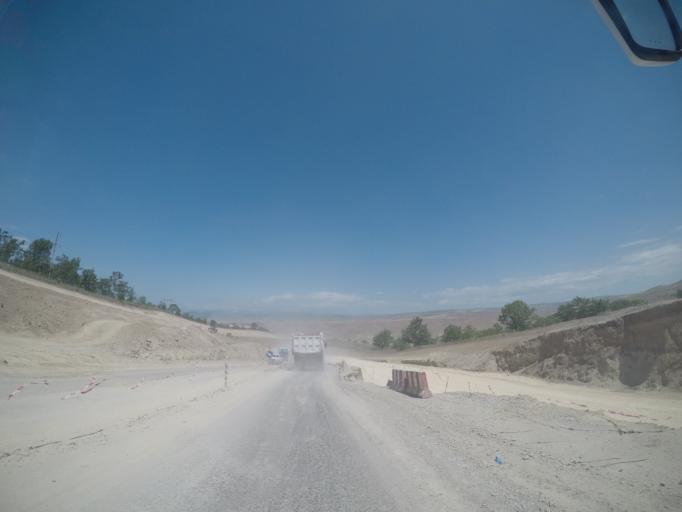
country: AZ
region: Qobustan
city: Qobustan
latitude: 40.5359
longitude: 48.7766
